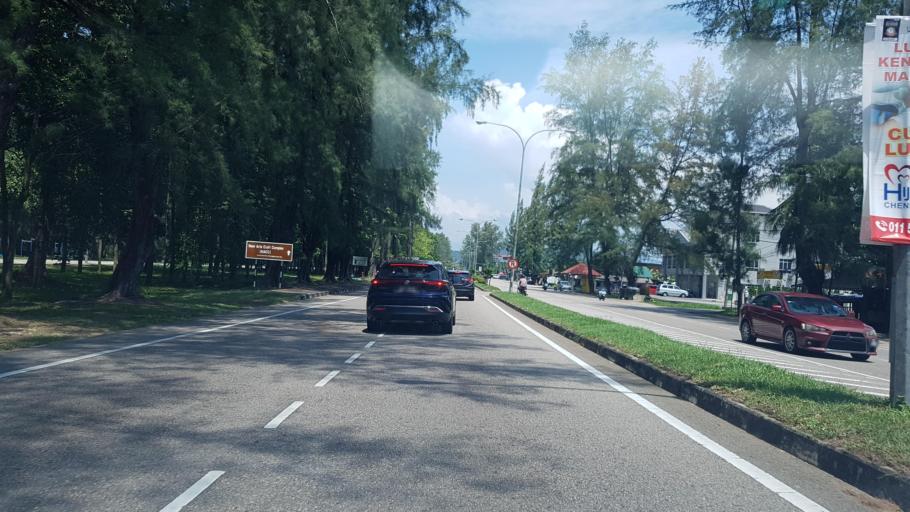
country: MY
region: Terengganu
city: Kuala Terengganu
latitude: 5.2884
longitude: 103.1688
